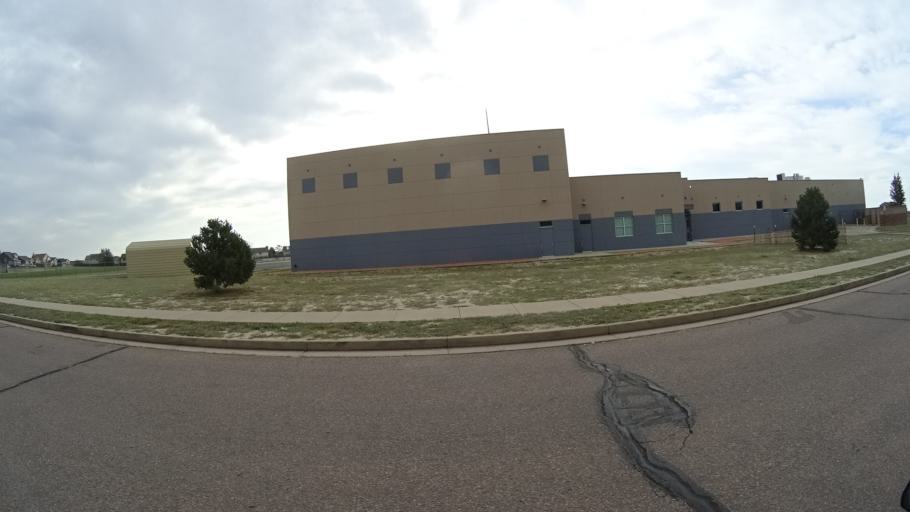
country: US
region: Colorado
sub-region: El Paso County
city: Cimarron Hills
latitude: 38.9212
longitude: -104.7111
